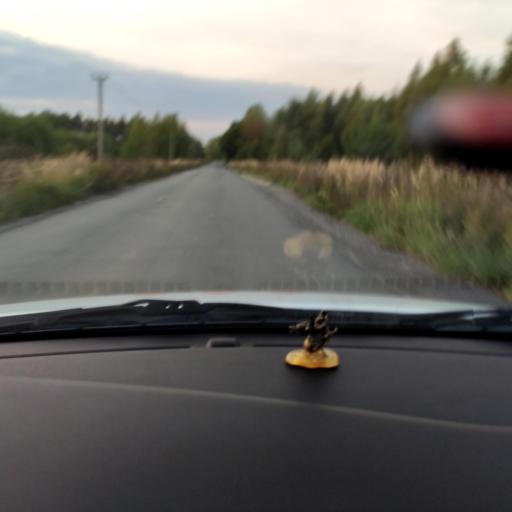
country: RU
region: Tatarstan
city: Vysokaya Gora
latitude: 55.8149
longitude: 49.3119
